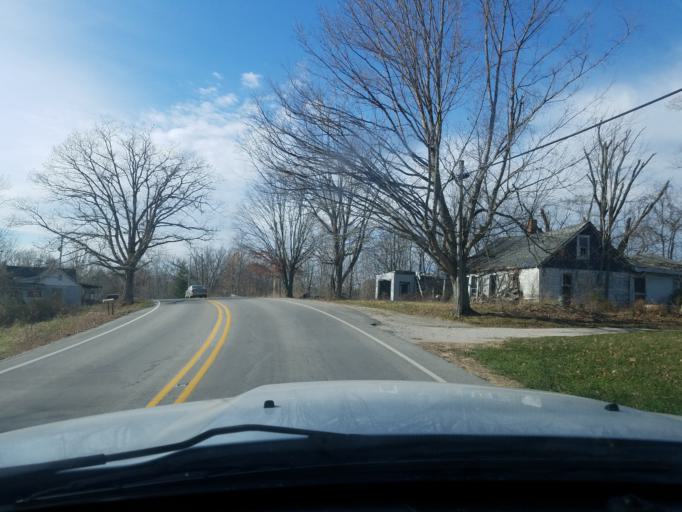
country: US
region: Indiana
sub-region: Orange County
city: Paoli
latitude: 38.5361
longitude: -86.4607
